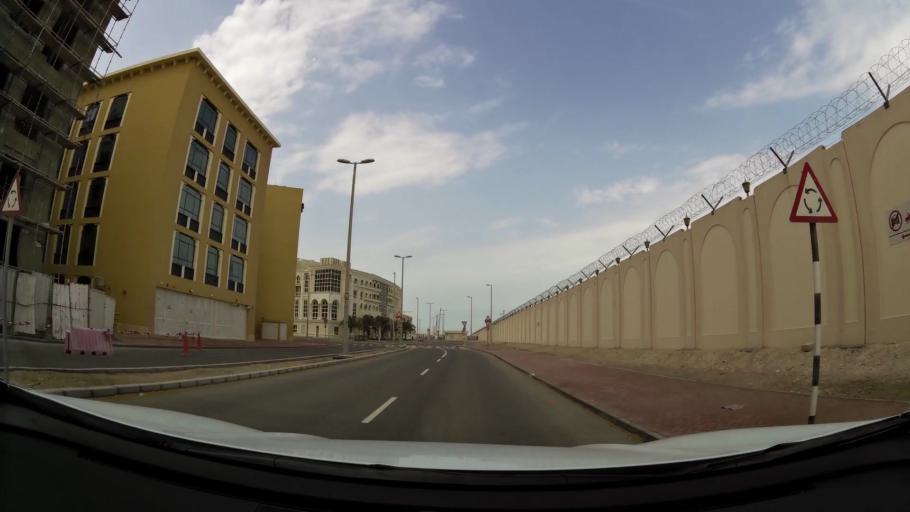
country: AE
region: Abu Dhabi
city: Abu Dhabi
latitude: 24.4188
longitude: 54.4673
